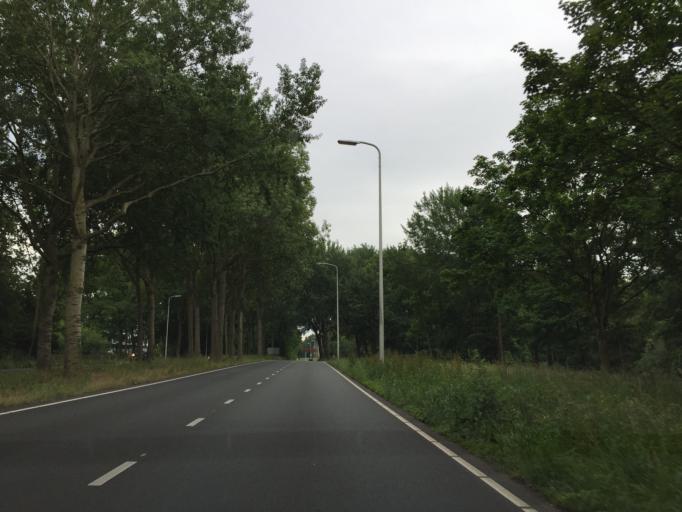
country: NL
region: South Holland
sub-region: Gemeente Westland
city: Poeldijk
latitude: 52.0488
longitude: 4.2313
